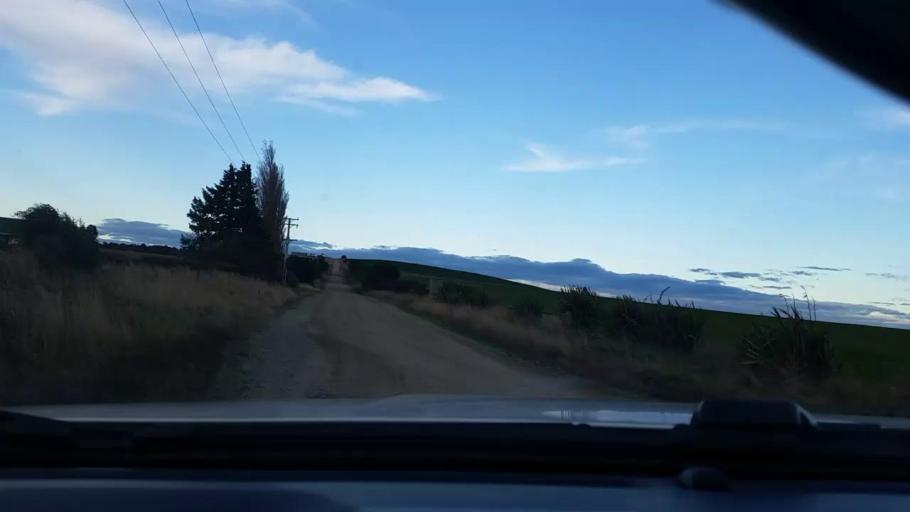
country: NZ
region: Southland
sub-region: Southland District
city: Winton
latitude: -46.0679
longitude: 168.4607
